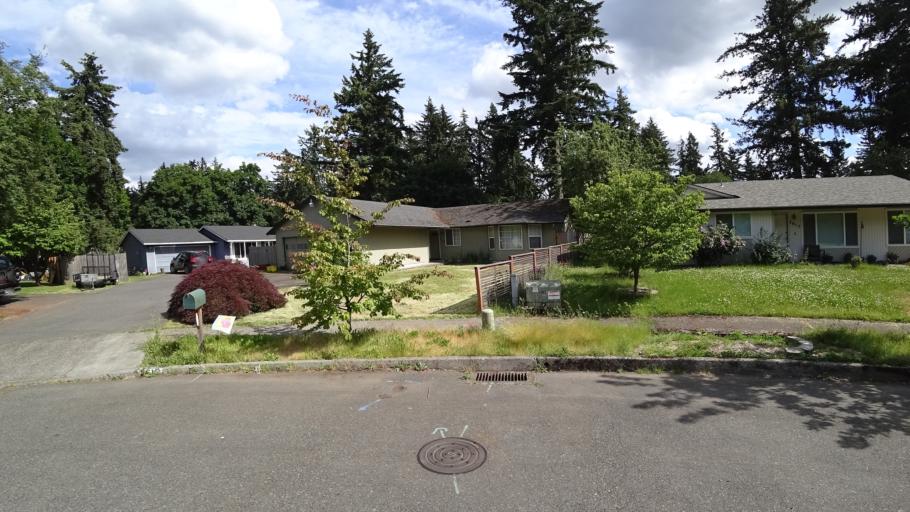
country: US
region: Oregon
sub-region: Multnomah County
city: Lents
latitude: 45.4961
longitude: -122.5419
